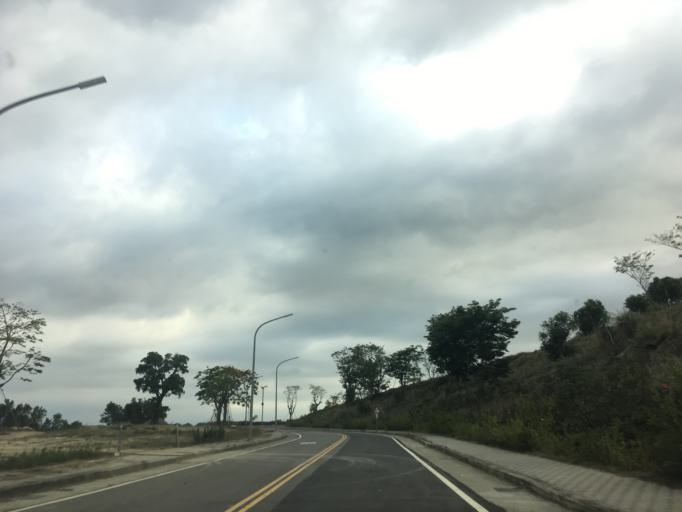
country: TW
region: Taiwan
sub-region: Taichung City
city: Taichung
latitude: 24.1742
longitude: 120.7687
